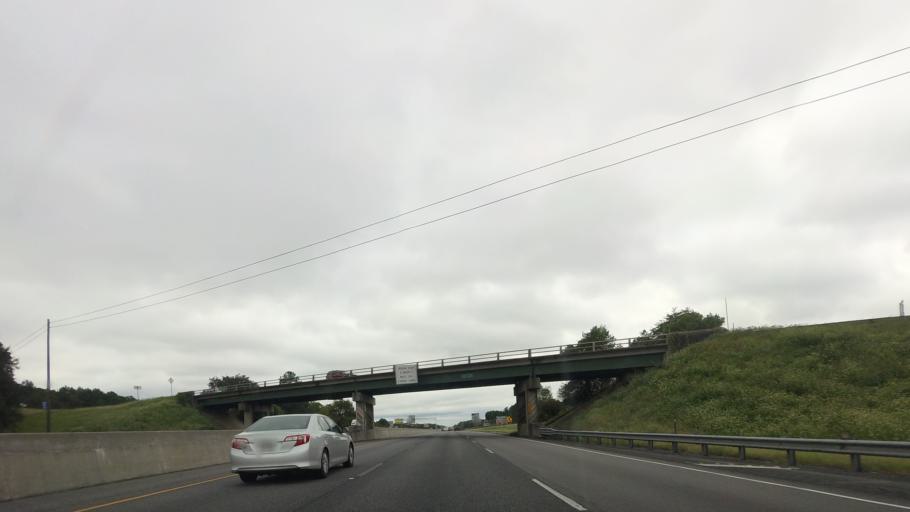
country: US
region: Georgia
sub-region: Lowndes County
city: Hahira
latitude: 30.9926
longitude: -83.3883
